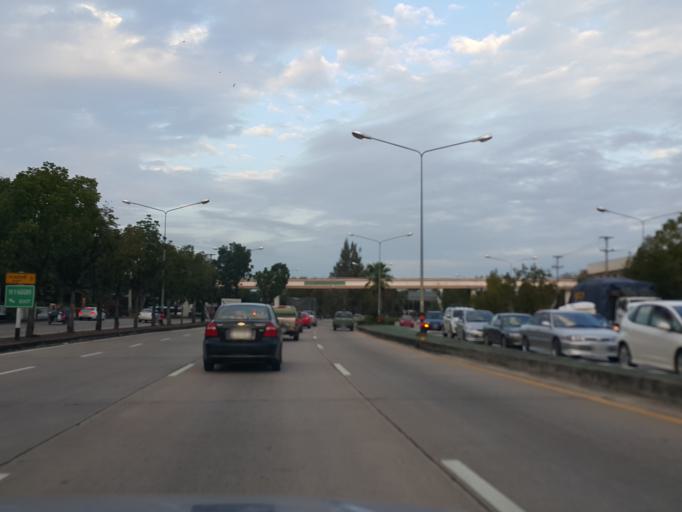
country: TH
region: Lampang
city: Lampang
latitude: 18.2801
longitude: 99.4891
